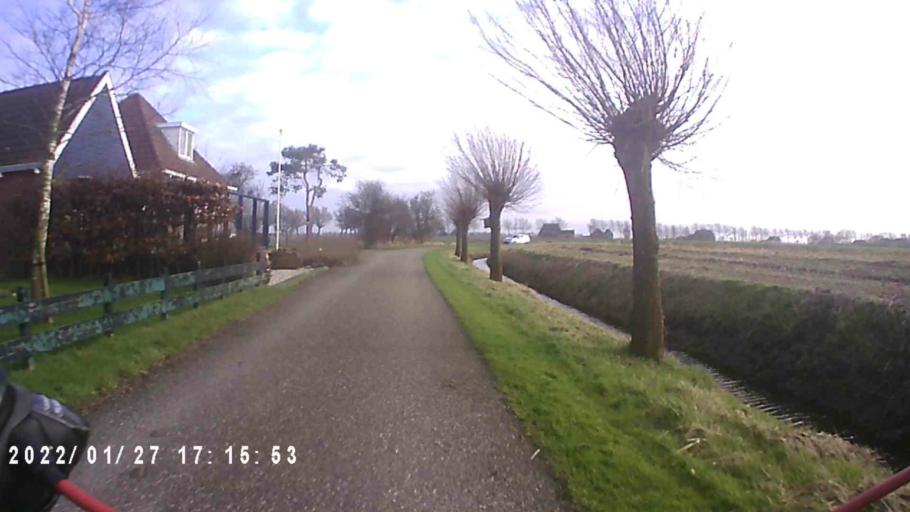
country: NL
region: Friesland
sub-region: Gemeente Dongeradeel
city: Anjum
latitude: 53.3923
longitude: 6.0977
